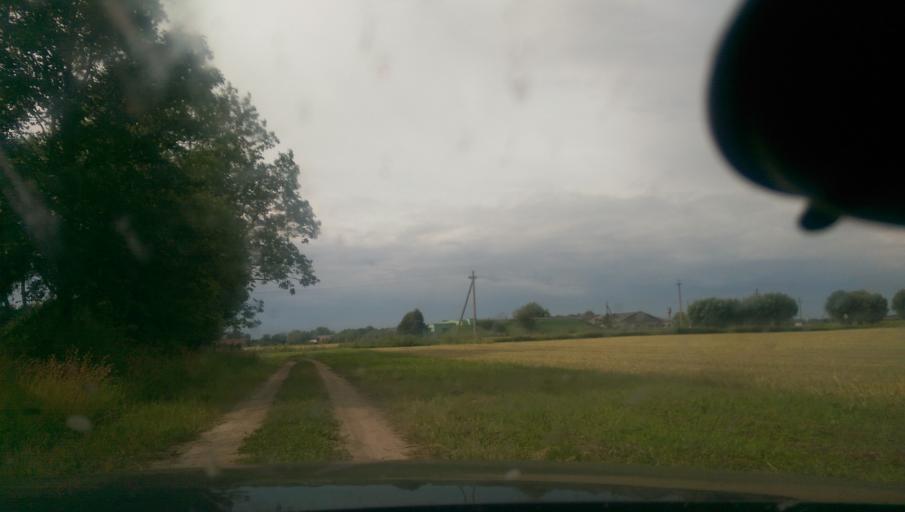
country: LT
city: Rusne
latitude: 55.2932
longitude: 21.3686
